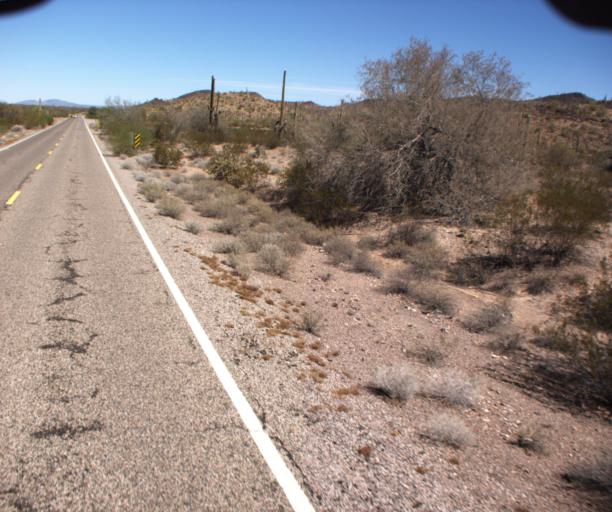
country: US
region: Arizona
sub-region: Pima County
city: Ajo
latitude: 32.2106
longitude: -112.7582
